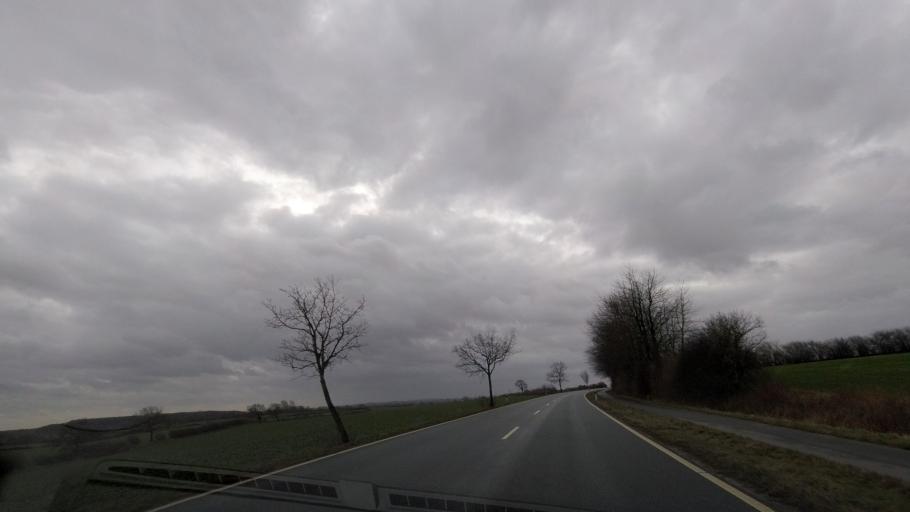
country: DE
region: Schleswig-Holstein
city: Tolk
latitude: 54.5700
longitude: 9.6453
